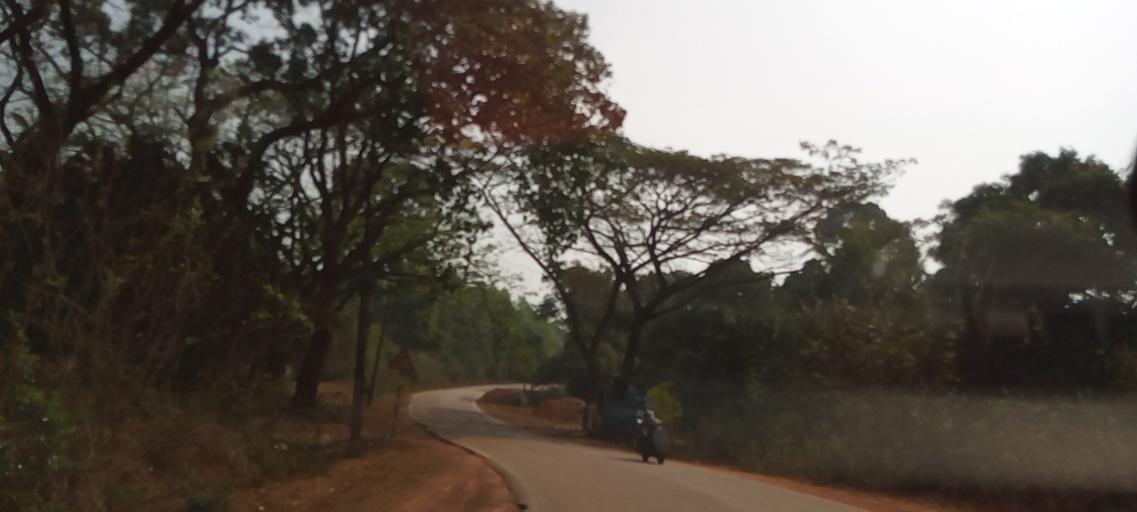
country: IN
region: Karnataka
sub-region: Udupi
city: Manipala
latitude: 13.5120
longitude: 74.8324
